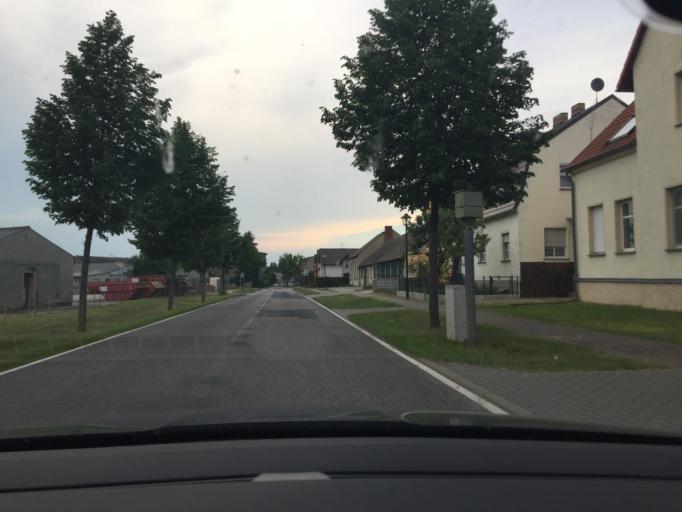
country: DE
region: Brandenburg
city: Niemegk
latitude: 52.0653
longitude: 12.6932
